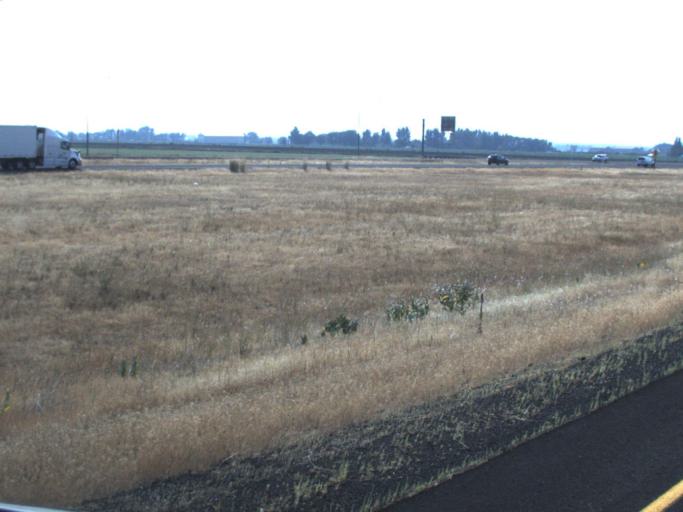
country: US
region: Washington
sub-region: Kittitas County
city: Ellensburg
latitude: 46.9659
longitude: -120.5098
